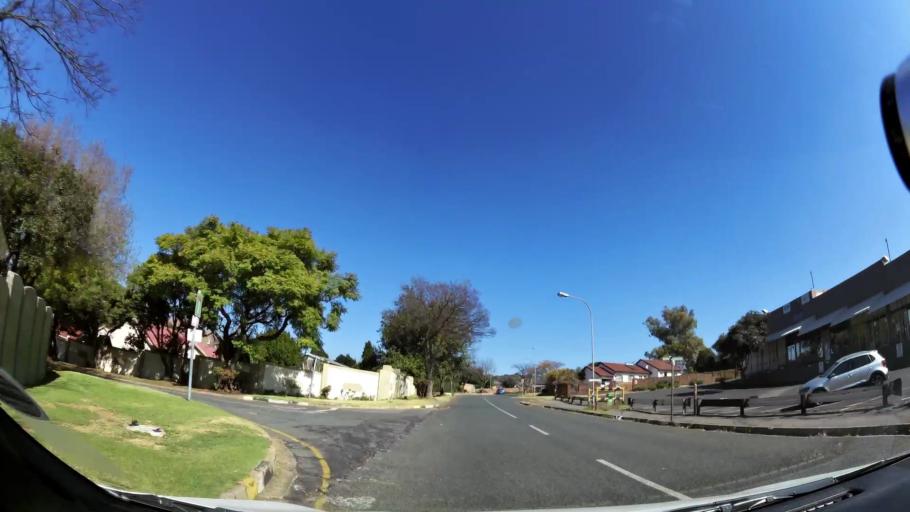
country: ZA
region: Gauteng
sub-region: City of Johannesburg Metropolitan Municipality
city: Johannesburg
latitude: -26.2756
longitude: 27.9856
